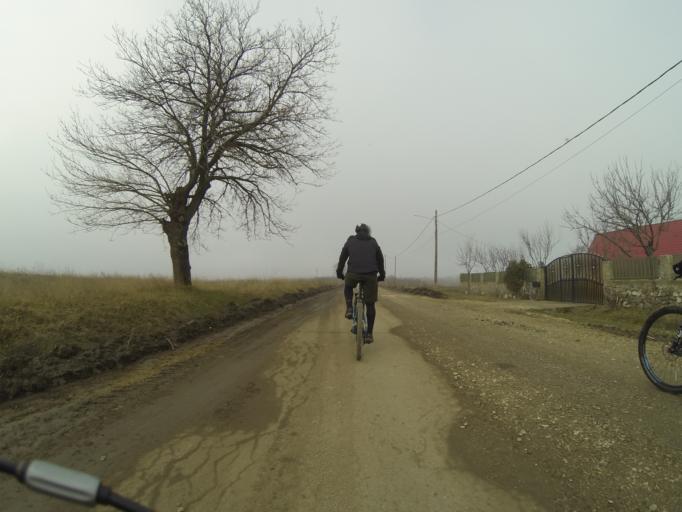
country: RO
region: Mehedinti
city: Dumbrava de Sus
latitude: 44.4900
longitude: 23.0958
